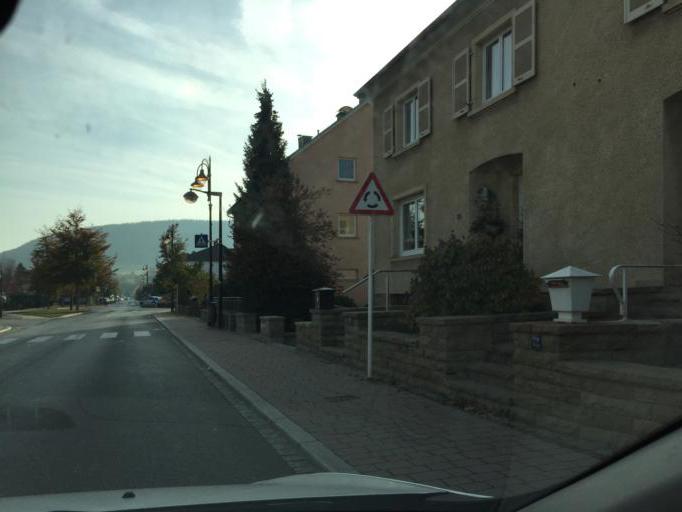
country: LU
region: Diekirch
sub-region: Canton de Diekirch
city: Diekirch
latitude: 49.8654
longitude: 6.1681
